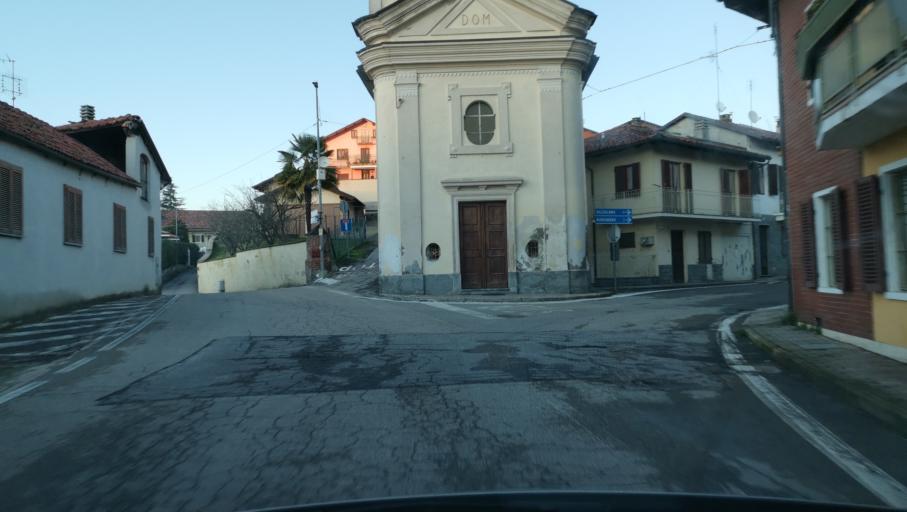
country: IT
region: Piedmont
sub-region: Provincia di Asti
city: Berzano di San Pietro
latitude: 45.0951
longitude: 7.9530
